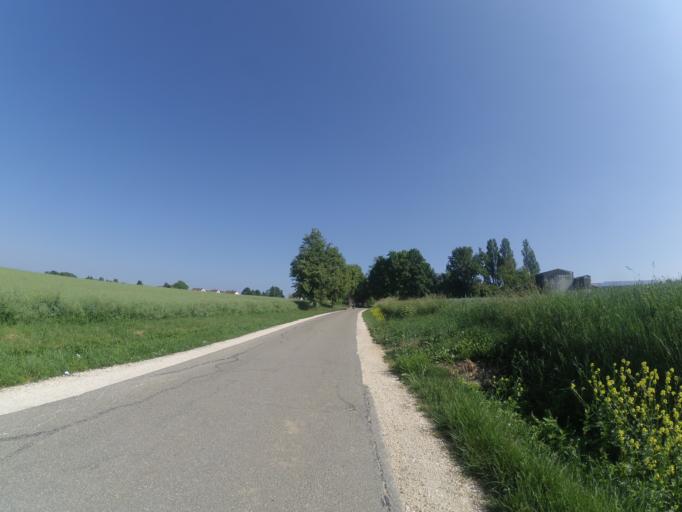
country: DE
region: Baden-Wuerttemberg
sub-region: Tuebingen Region
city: Beimerstetten
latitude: 48.4775
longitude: 9.9890
